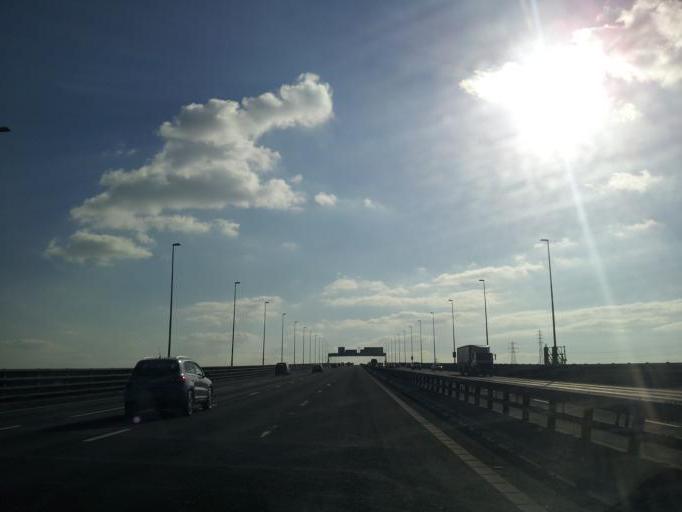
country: GB
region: England
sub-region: North Somerset
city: Easton-in-Gordano
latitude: 51.4941
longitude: -2.6873
